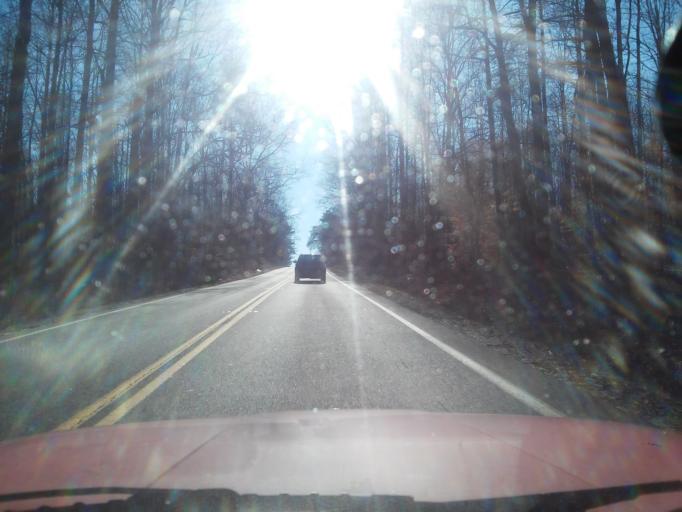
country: US
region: Virginia
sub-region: Orange County
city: Gordonsville
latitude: 37.9988
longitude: -78.1946
